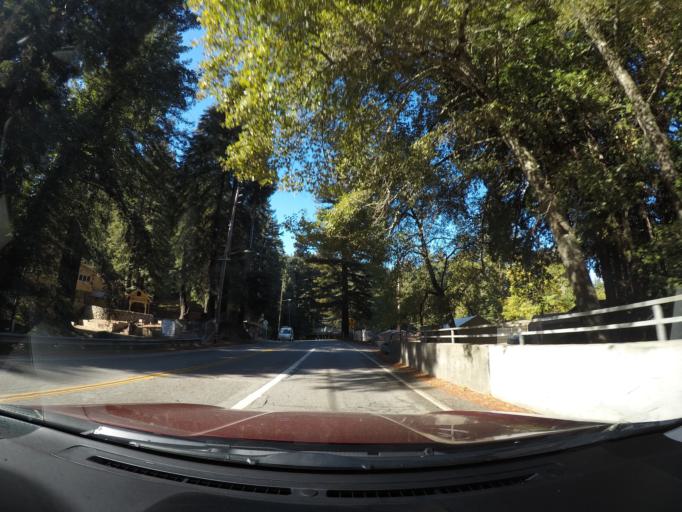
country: US
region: California
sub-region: Santa Cruz County
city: Brookdale
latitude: 37.1079
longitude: -122.1090
